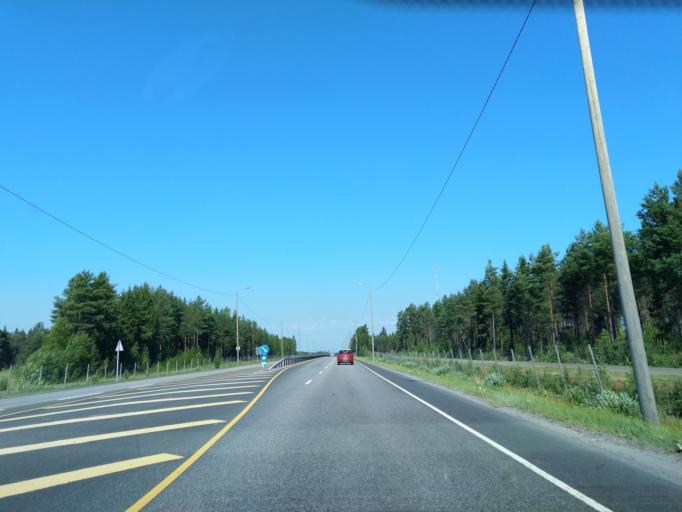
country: FI
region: Satakunta
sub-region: Pori
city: Nakkila
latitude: 61.3334
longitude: 22.0559
